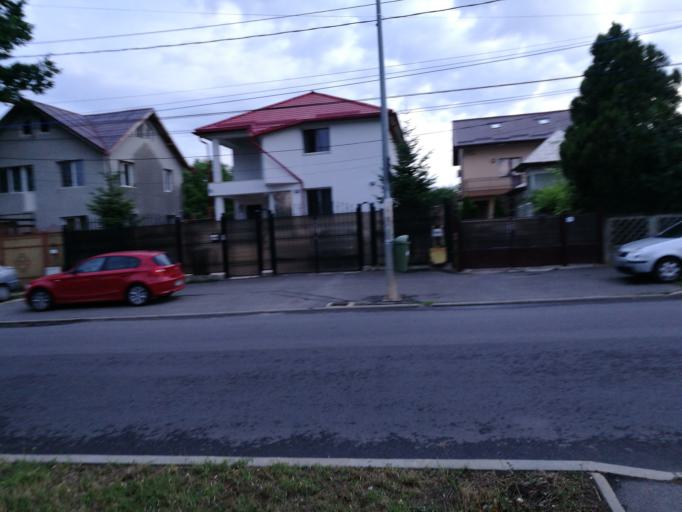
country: RO
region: Ilfov
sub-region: Comuna Otopeni
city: Otopeni
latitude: 44.5039
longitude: 26.0580
